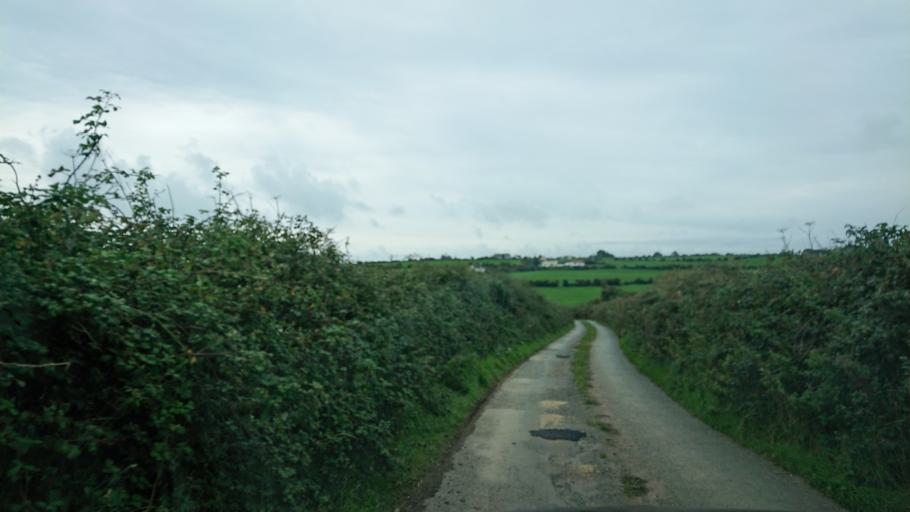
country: IE
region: Munster
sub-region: Waterford
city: Dunmore East
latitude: 52.1742
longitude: -6.9949
